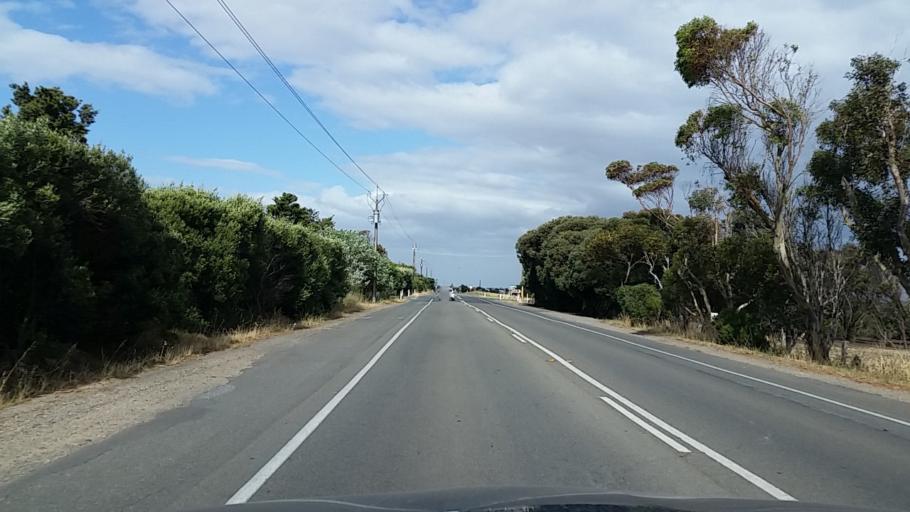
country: AU
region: South Australia
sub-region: Alexandrina
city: Port Elliot
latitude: -35.5119
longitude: 138.6976
